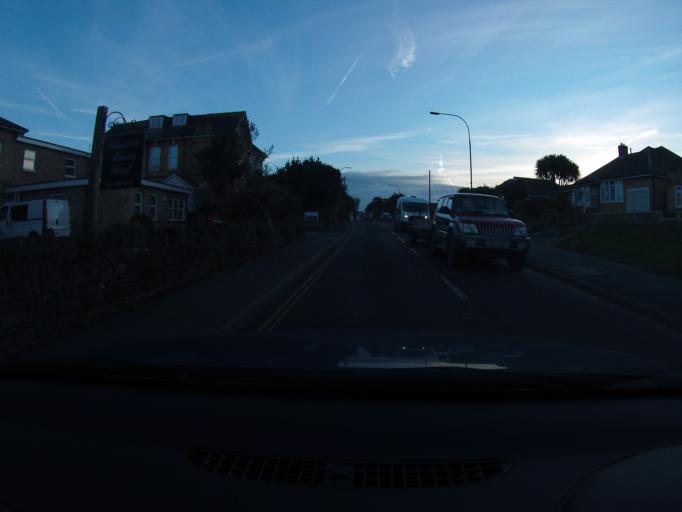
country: GB
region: England
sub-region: Isle of Wight
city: Sandown
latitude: 50.6582
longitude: -1.1567
